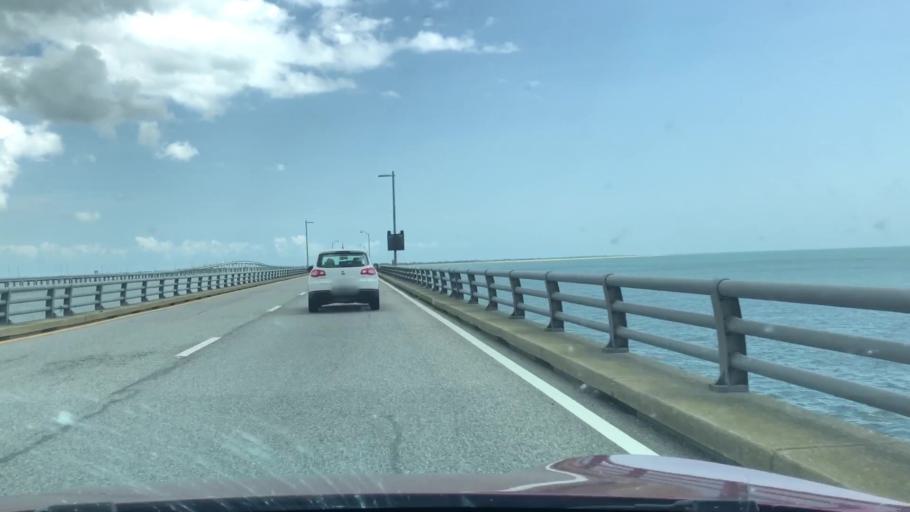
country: US
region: Virginia
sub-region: Northampton County
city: Cape Charles
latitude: 37.0827
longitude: -76.0082
